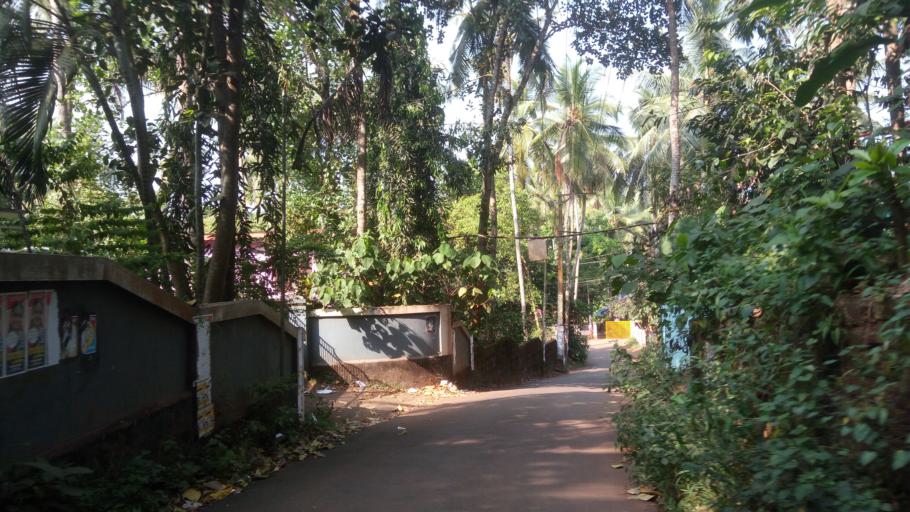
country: IN
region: Kerala
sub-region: Malappuram
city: Malappuram
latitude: 10.9937
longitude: 75.9996
